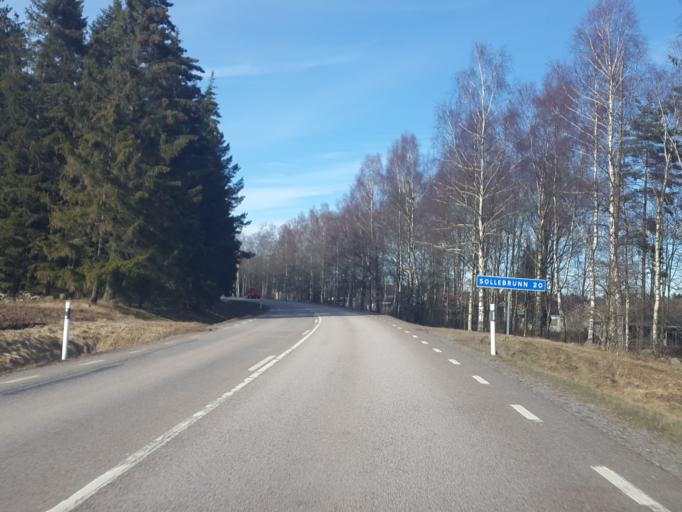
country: SE
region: Vaestra Goetaland
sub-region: Vargarda Kommun
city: Jonstorp
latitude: 58.0219
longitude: 12.6348
